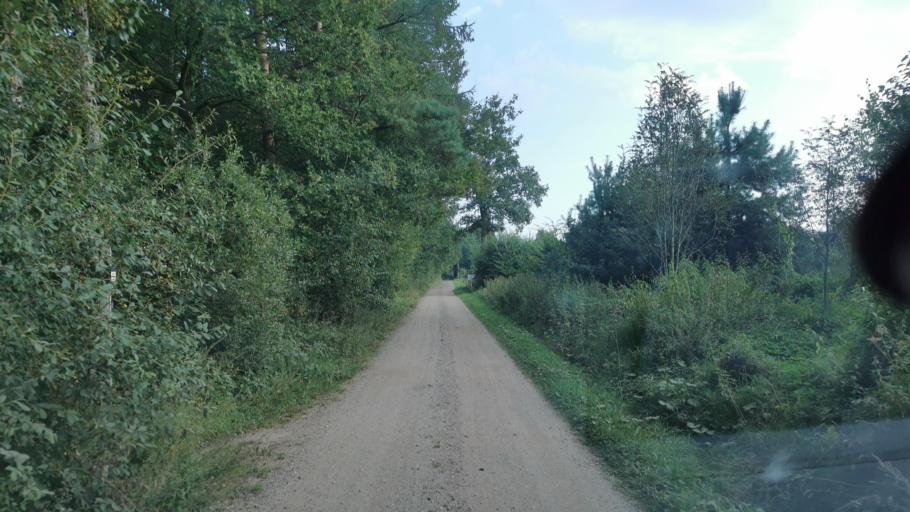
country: NL
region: Overijssel
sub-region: Gemeente Losser
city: Losser
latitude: 52.2933
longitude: 6.9787
